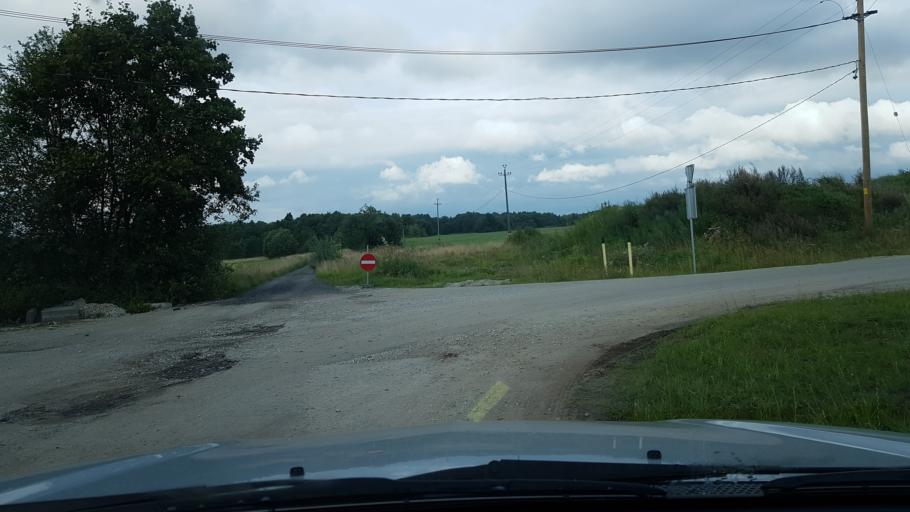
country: EE
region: Harju
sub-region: Rae vald
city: Jueri
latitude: 59.3769
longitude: 24.8576
